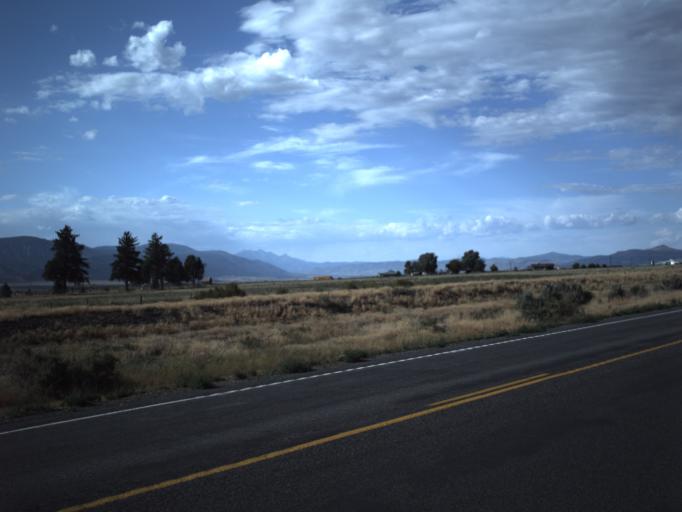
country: US
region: Utah
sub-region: Sanpete County
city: Ephraim
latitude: 39.3879
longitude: -111.5812
